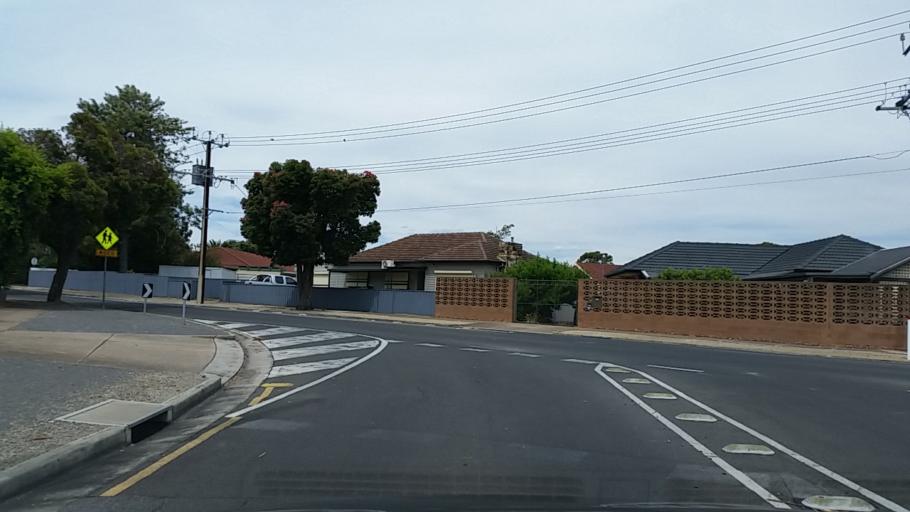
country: AU
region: South Australia
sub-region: City of West Torrens
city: Plympton
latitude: -34.9550
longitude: 138.5488
